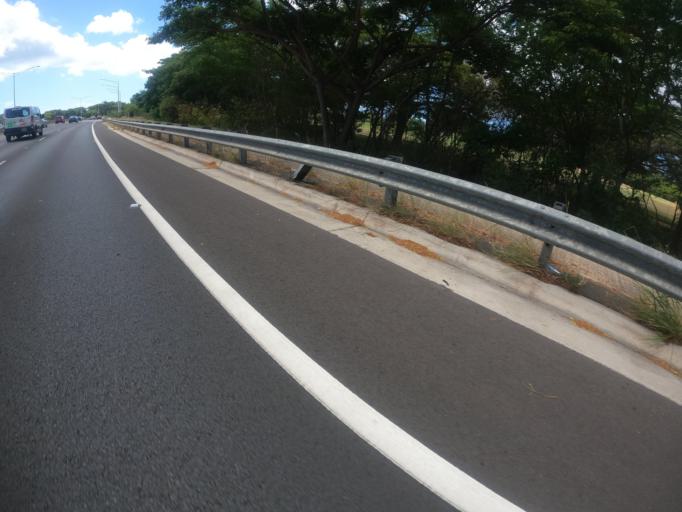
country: US
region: Hawaii
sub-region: Honolulu County
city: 'Ewa Gentry
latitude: 21.3656
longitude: -158.0267
